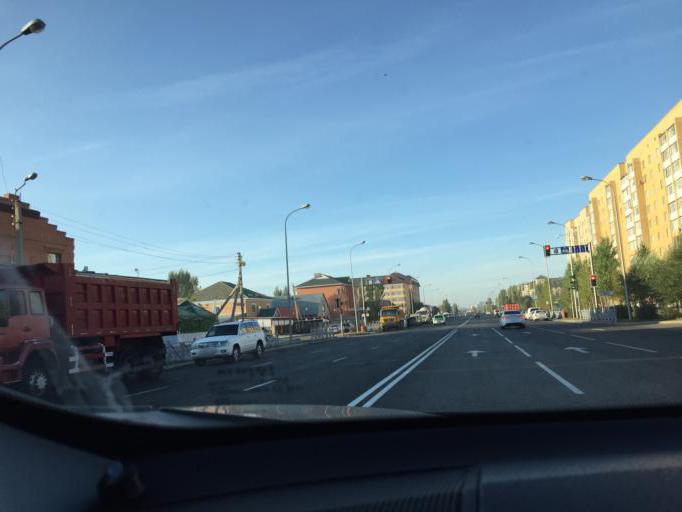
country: KZ
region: Astana Qalasy
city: Astana
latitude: 51.1557
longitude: 71.5115
